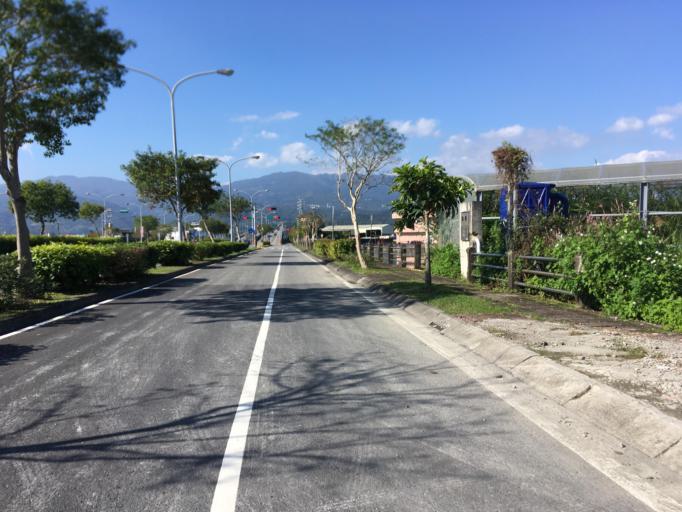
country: TW
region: Taiwan
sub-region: Yilan
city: Yilan
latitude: 24.7724
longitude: 121.7660
